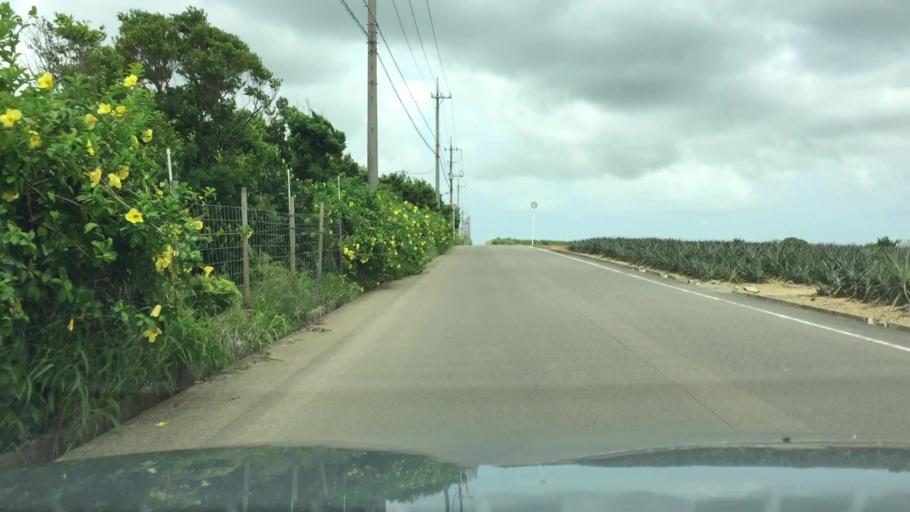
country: JP
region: Okinawa
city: Ishigaki
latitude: 24.3954
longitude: 124.1779
